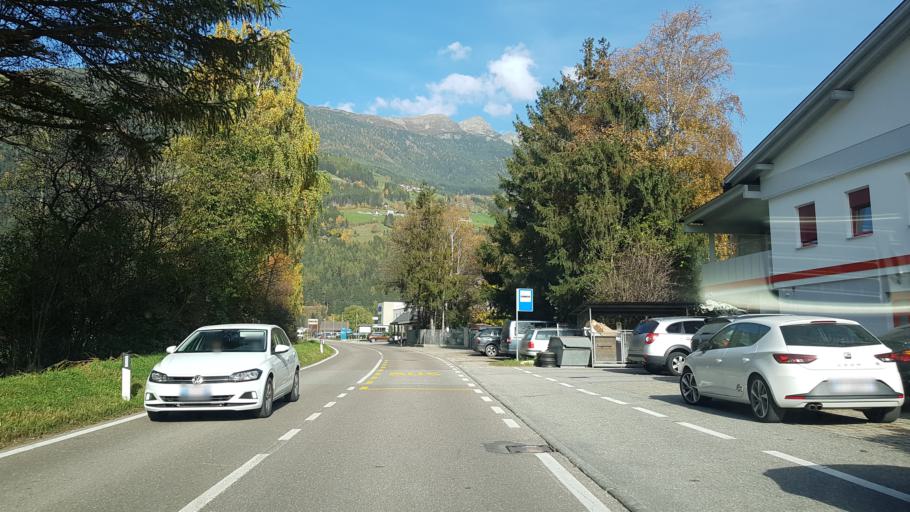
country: IT
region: Trentino-Alto Adige
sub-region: Bolzano
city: Campo Tures
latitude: 46.9085
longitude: 11.9591
